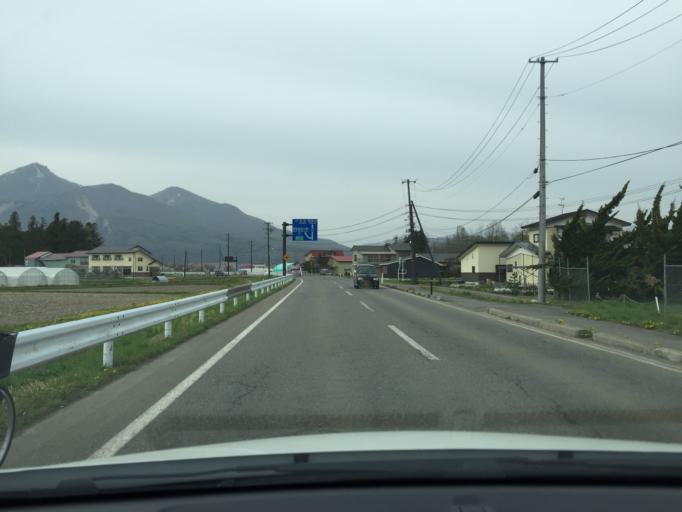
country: JP
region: Fukushima
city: Inawashiro
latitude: 37.5469
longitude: 140.1262
